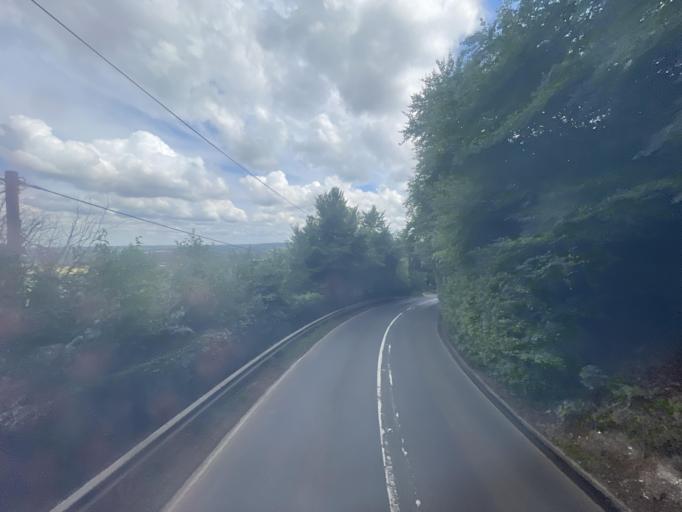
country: GB
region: England
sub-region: Kent
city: Westerham
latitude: 51.2868
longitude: 0.0643
